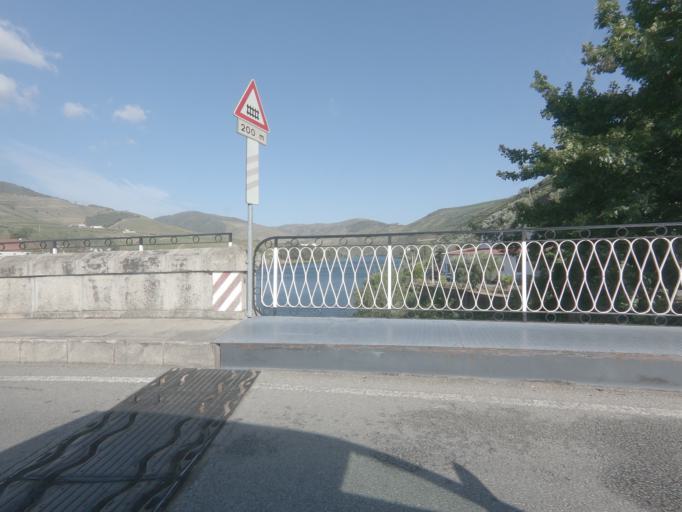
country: PT
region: Vila Real
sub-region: Sabrosa
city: Vilela
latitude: 41.1877
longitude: -7.5431
